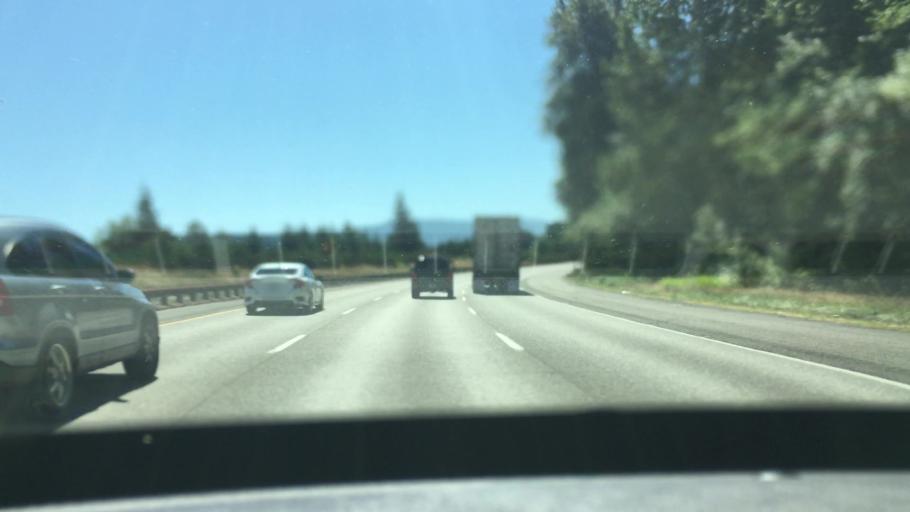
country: US
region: Washington
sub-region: King County
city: Fall City
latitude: 47.5308
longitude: -121.9435
